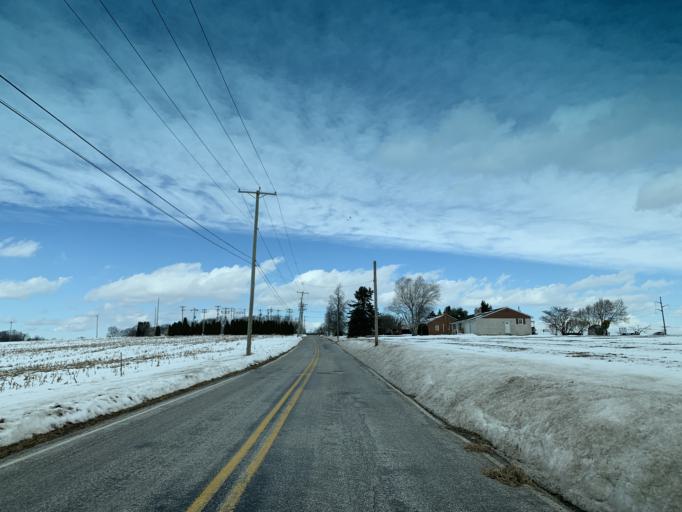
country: US
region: Pennsylvania
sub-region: York County
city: Stewartstown
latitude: 39.7680
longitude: -76.6334
